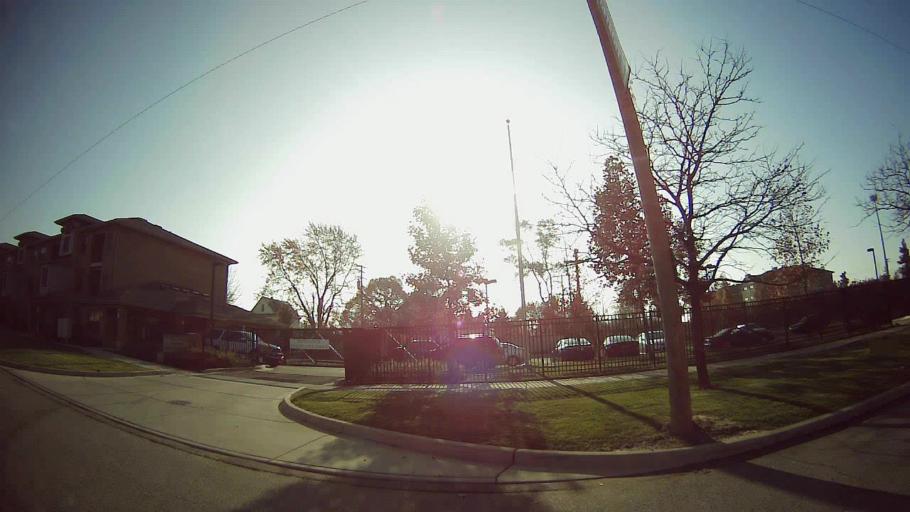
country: US
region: Michigan
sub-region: Wayne County
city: Highland Park
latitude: 42.4026
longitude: -83.1132
